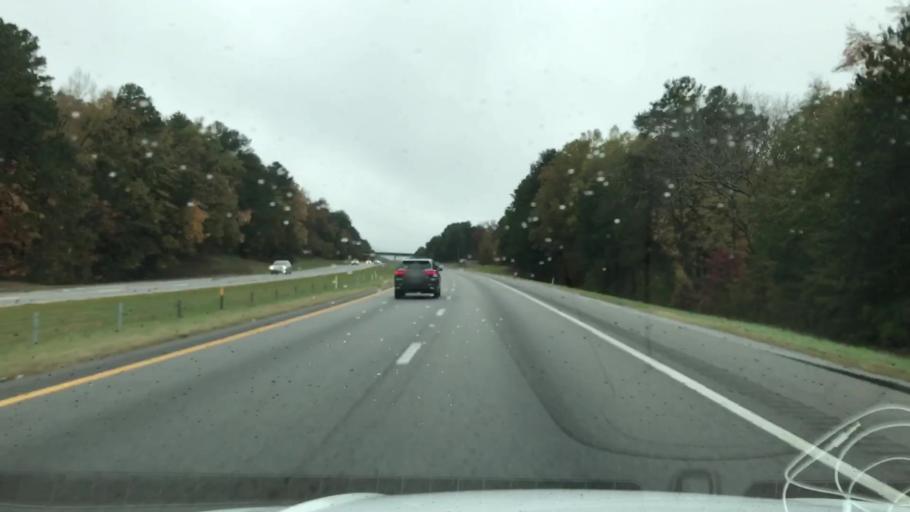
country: US
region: South Carolina
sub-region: Richland County
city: Lake Murray of Richland
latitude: 34.1342
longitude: -81.2120
